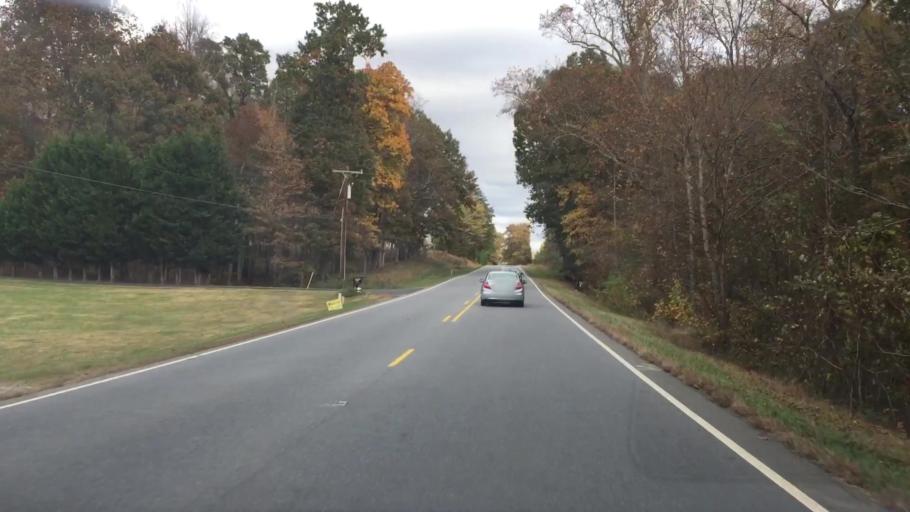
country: US
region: North Carolina
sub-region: Guilford County
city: Summerfield
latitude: 36.2654
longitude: -79.8550
